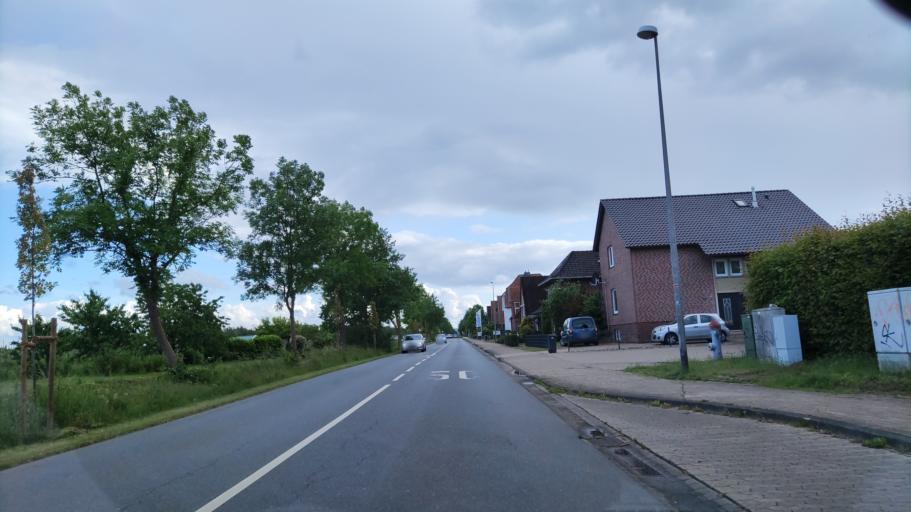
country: DE
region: Lower Saxony
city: Jork
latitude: 53.5284
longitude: 9.6780
